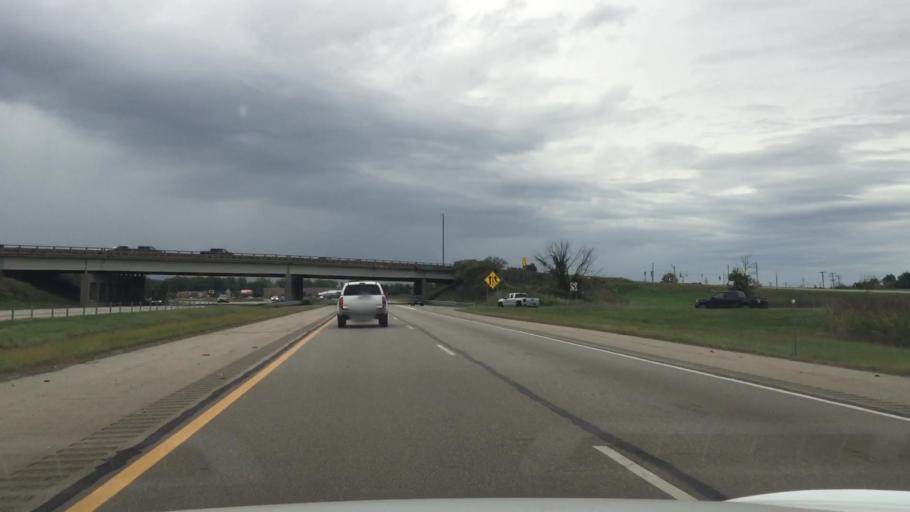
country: US
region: Michigan
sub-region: Macomb County
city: New Haven
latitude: 42.6754
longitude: -82.8193
